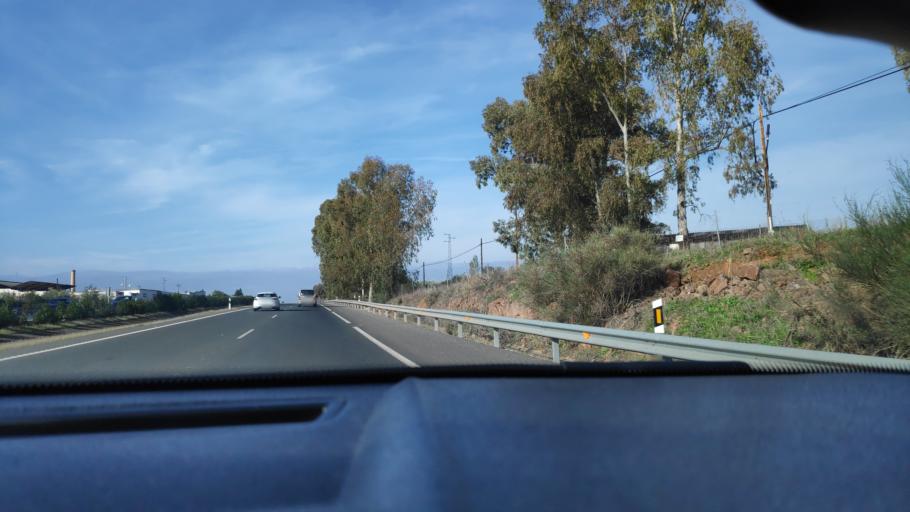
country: ES
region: Andalusia
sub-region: Provincia de Jaen
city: Linares
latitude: 38.0948
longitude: -3.6888
